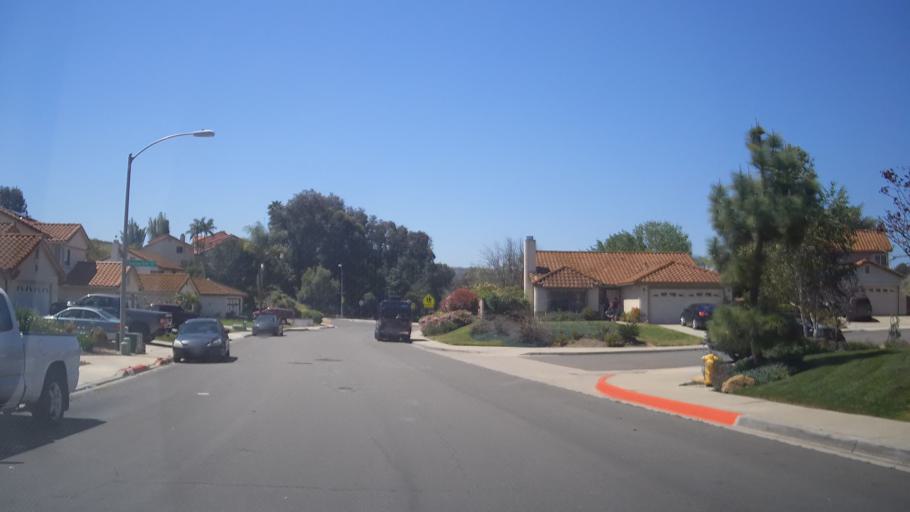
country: US
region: California
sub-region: San Diego County
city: Poway
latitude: 32.9549
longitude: -117.0941
